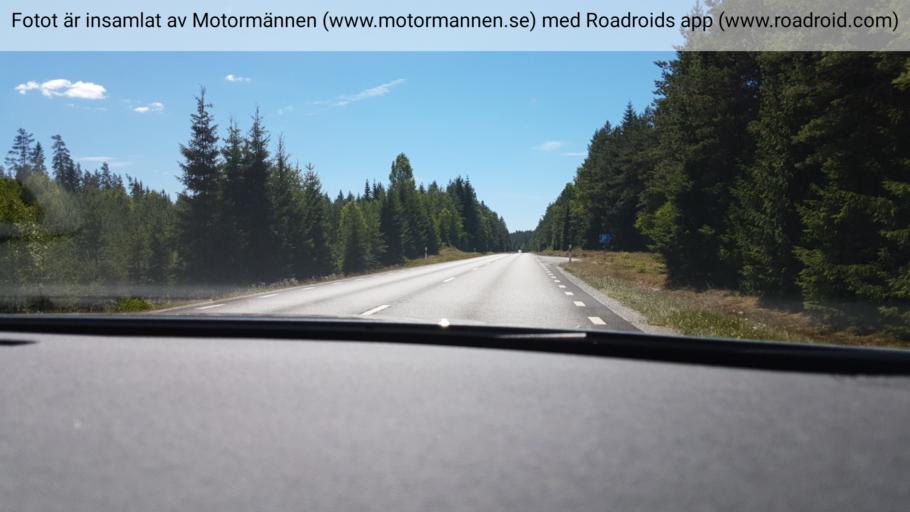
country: SE
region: Joenkoeping
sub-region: Gnosjo Kommun
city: Gnosjoe
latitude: 57.5838
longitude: 13.7230
